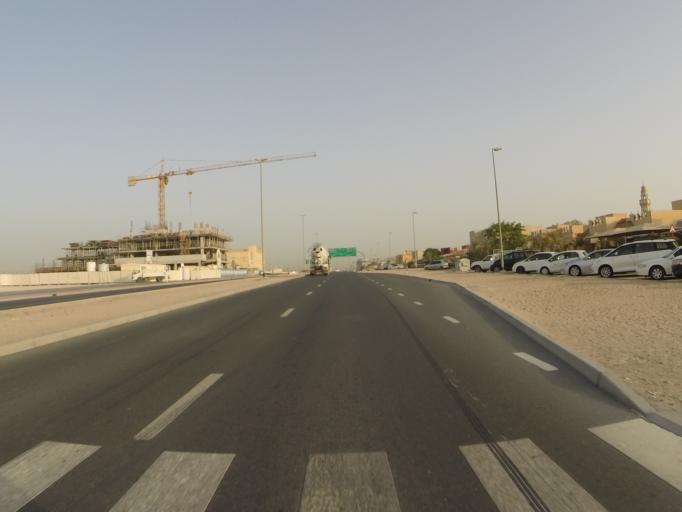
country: AE
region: Dubai
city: Dubai
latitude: 25.1622
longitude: 55.2494
